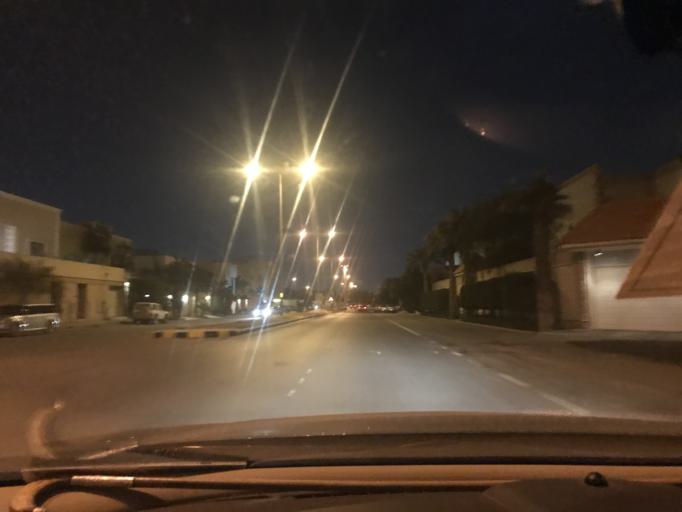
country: SA
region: Ar Riyad
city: Riyadh
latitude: 24.7603
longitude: 46.7439
